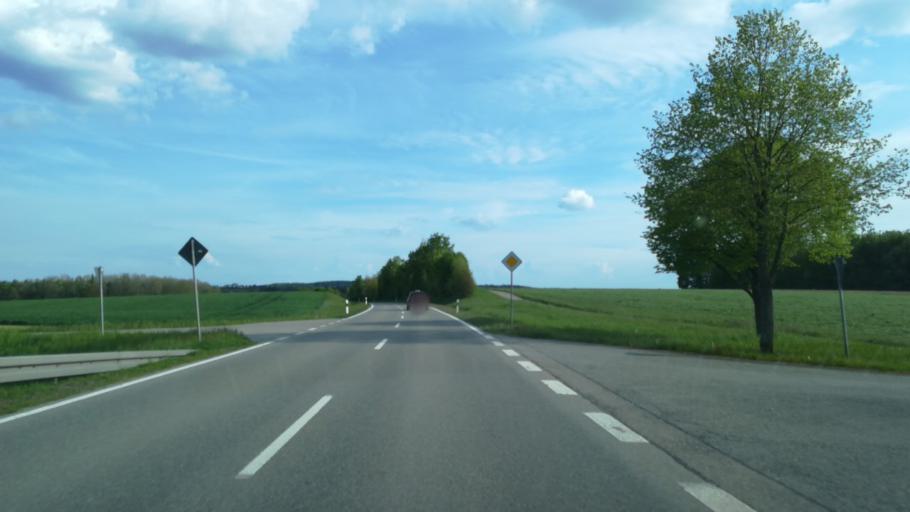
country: DE
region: Baden-Wuerttemberg
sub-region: Freiburg Region
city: Muhlingen
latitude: 47.9304
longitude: 9.0482
